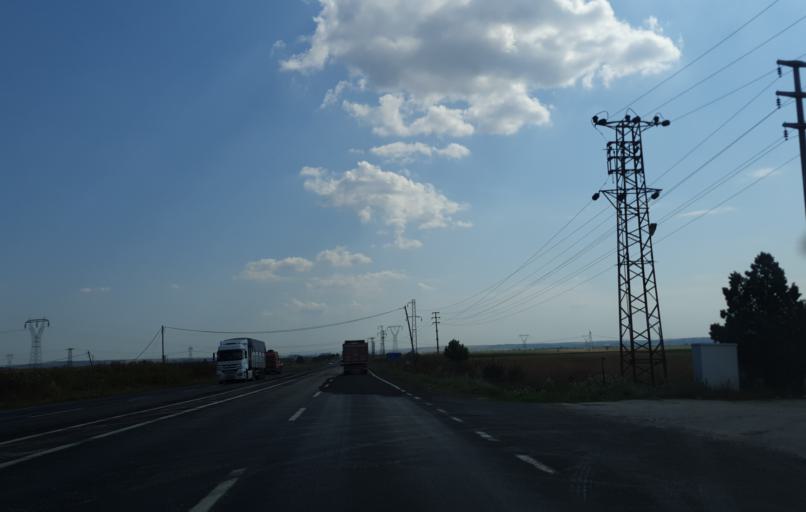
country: TR
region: Kirklareli
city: Buyukkaristiran
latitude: 41.2449
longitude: 27.5394
